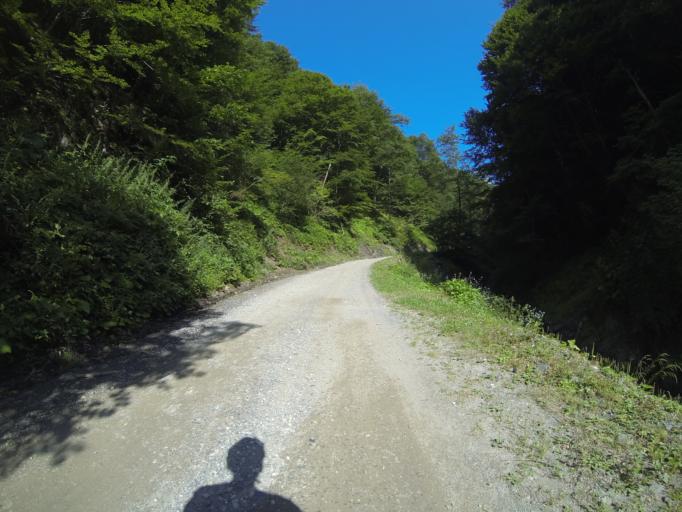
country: RO
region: Valcea
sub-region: Comuna Costesti
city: Bistrita
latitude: 45.2145
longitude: 24.0073
